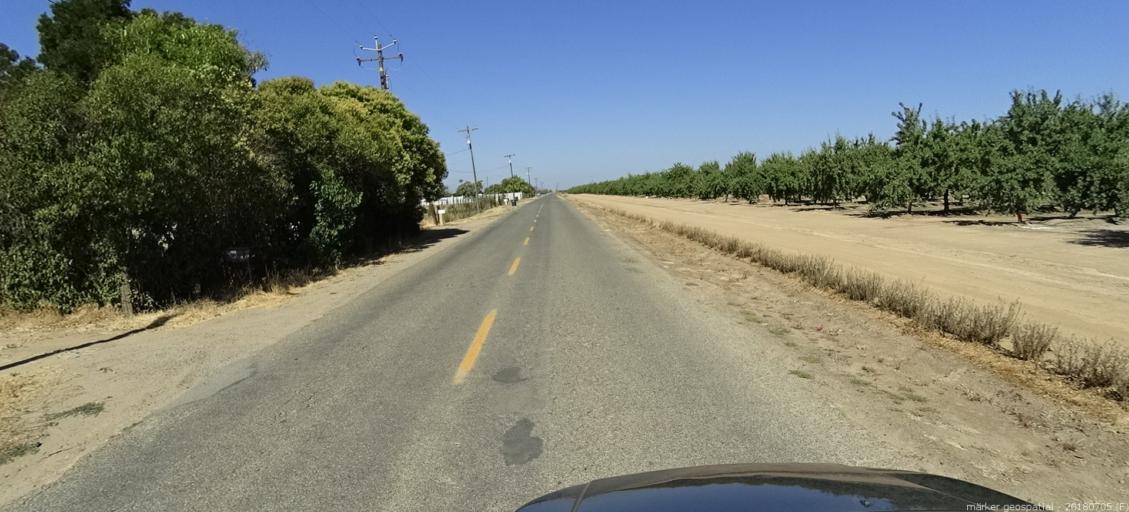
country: US
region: California
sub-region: Madera County
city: Madera Acres
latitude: 37.0980
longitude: -120.1050
